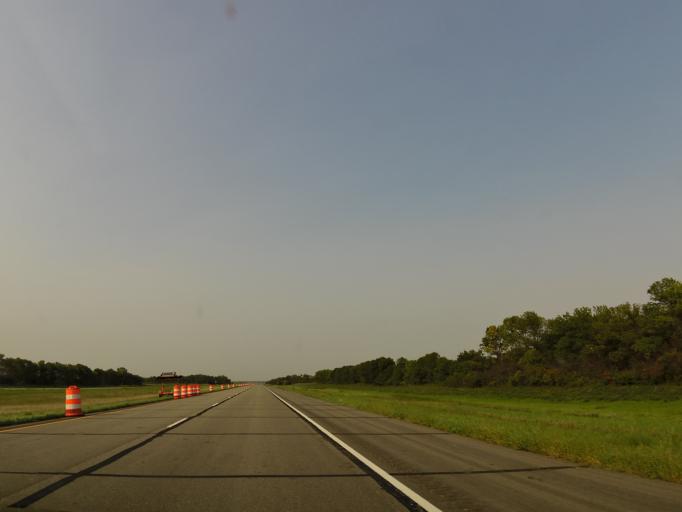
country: US
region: North Dakota
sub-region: Cass County
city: Horace
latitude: 46.5292
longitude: -96.8299
